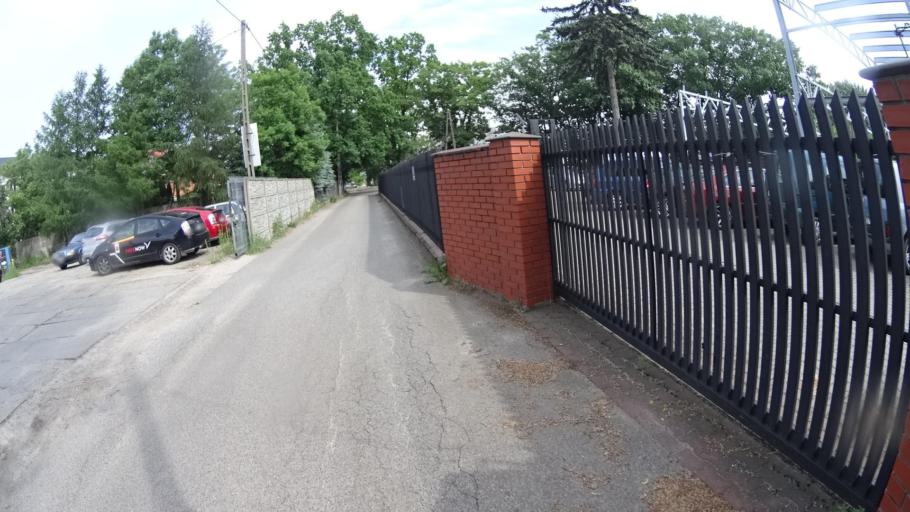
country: PL
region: Masovian Voivodeship
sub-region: Warszawa
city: Wlochy
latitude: 52.1870
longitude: 20.9240
